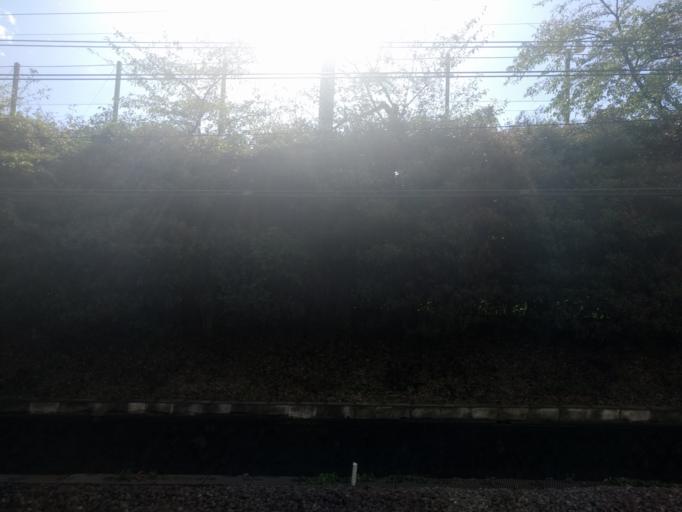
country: JP
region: Tokyo
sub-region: Machida-shi
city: Machida
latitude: 35.5668
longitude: 139.4668
